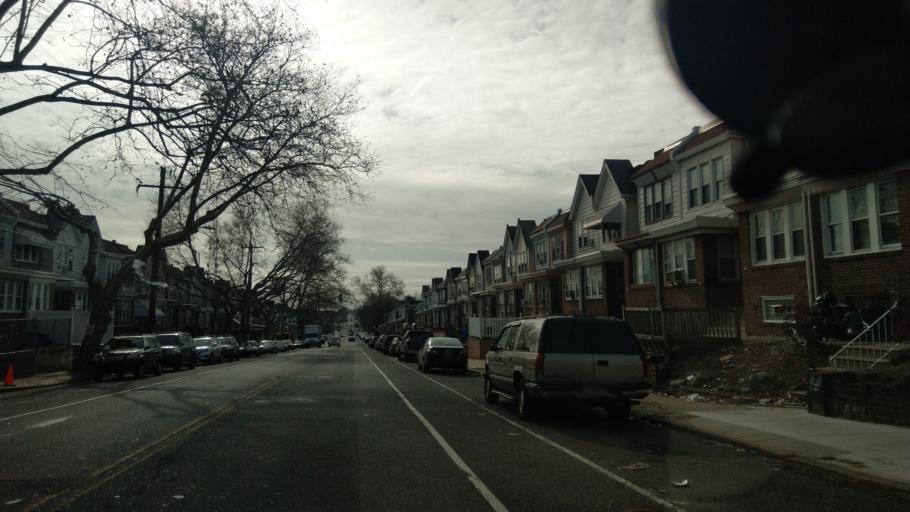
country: US
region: Pennsylvania
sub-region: Montgomery County
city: Rockledge
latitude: 40.0195
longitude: -75.1106
